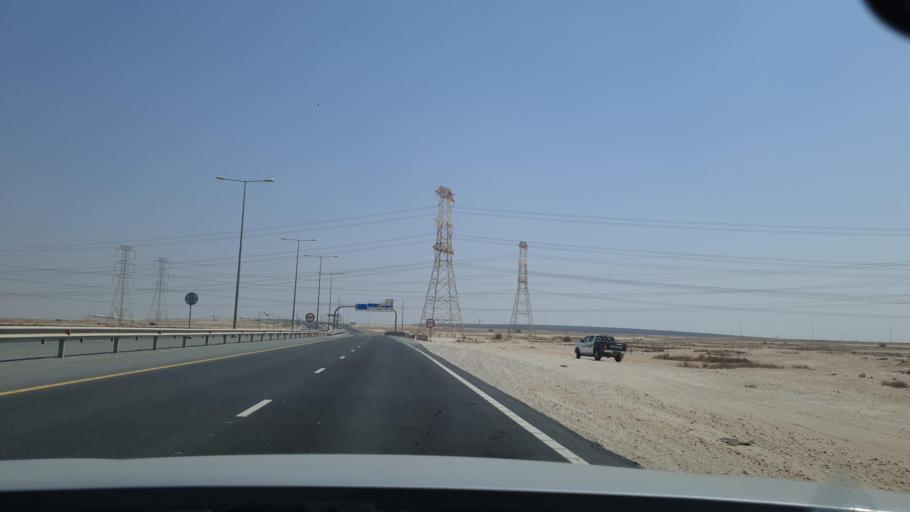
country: QA
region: Baladiyat az Za`ayin
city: Az Za`ayin
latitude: 25.6194
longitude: 51.3525
